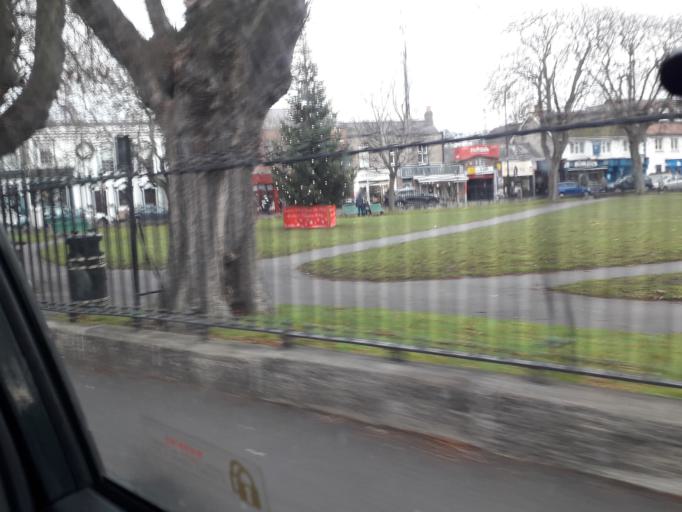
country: IE
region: Leinster
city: Sandymount
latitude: 53.3319
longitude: -6.2157
